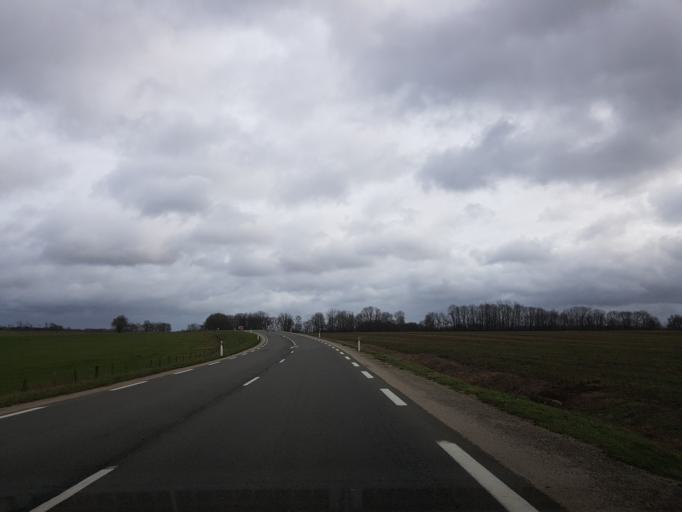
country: FR
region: Champagne-Ardenne
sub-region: Departement de la Haute-Marne
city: Chalindrey
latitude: 47.8440
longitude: 5.4532
